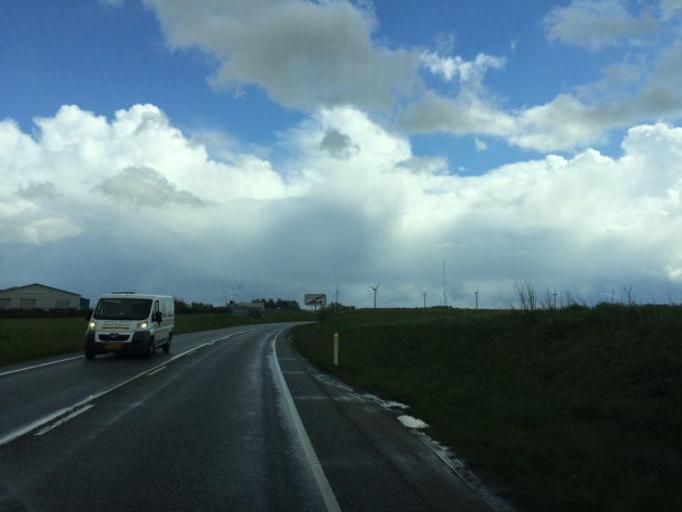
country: DK
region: Central Jutland
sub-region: Holstebro Kommune
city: Holstebro
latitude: 56.3777
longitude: 8.6353
